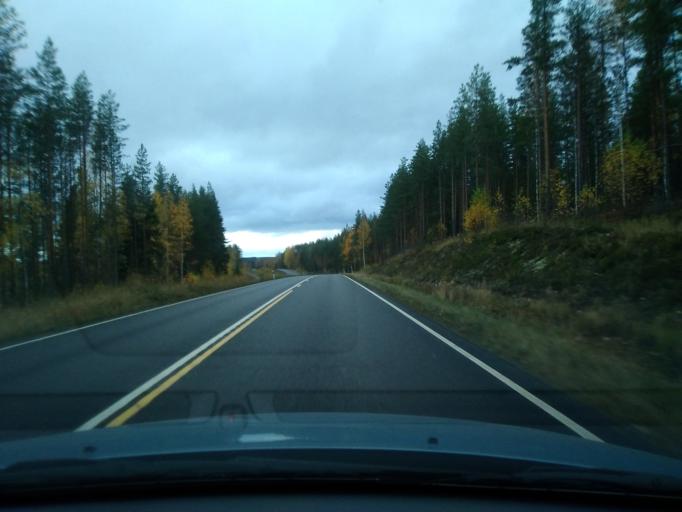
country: FI
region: Central Finland
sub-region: Jyvaeskylae
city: Uurainen
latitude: 62.6246
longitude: 25.5392
